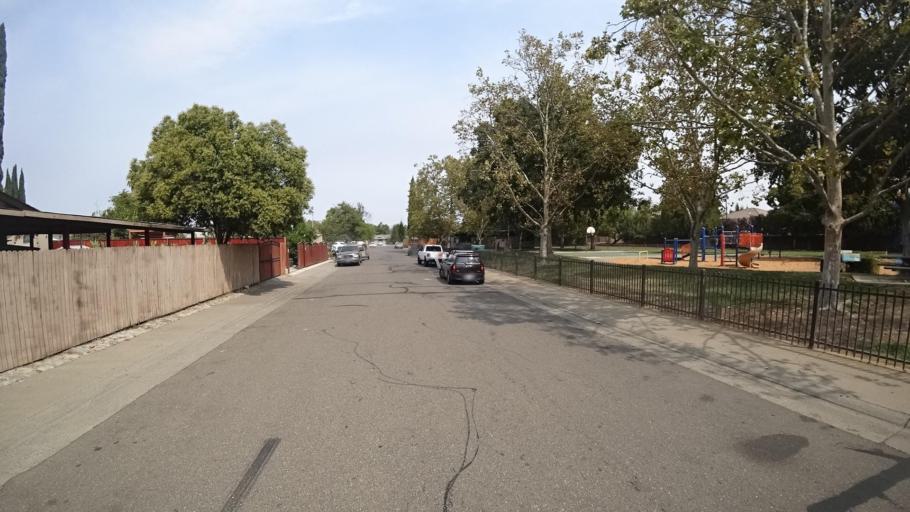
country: US
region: California
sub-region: Sacramento County
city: Elk Grove
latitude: 38.4218
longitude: -121.3771
